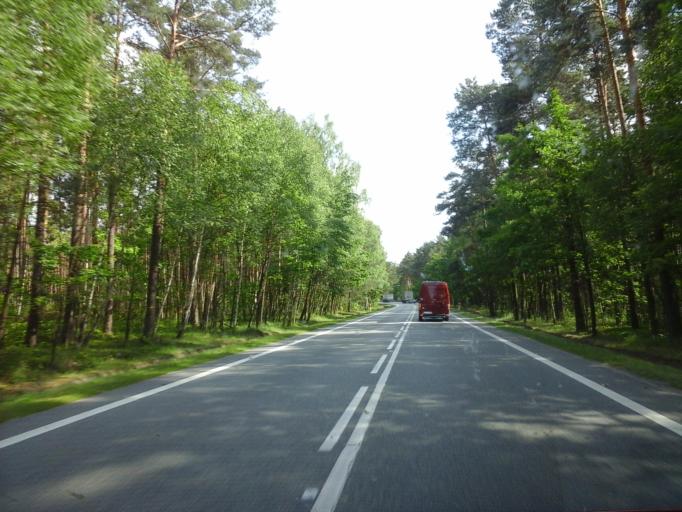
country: PL
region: Swietokrzyskie
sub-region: Powiat konecki
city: Ruda Maleniecka
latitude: 51.1692
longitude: 20.2225
